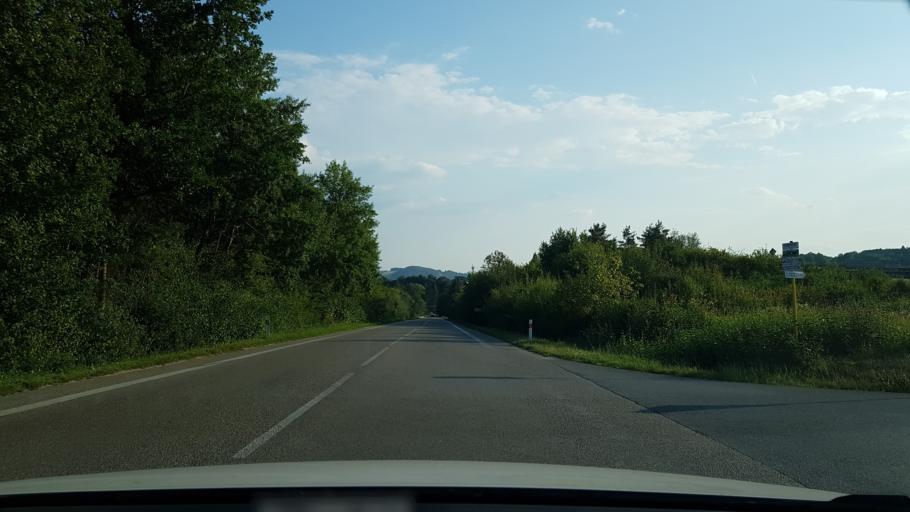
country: SK
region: Zilinsky
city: Bytca
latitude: 49.2023
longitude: 18.5132
